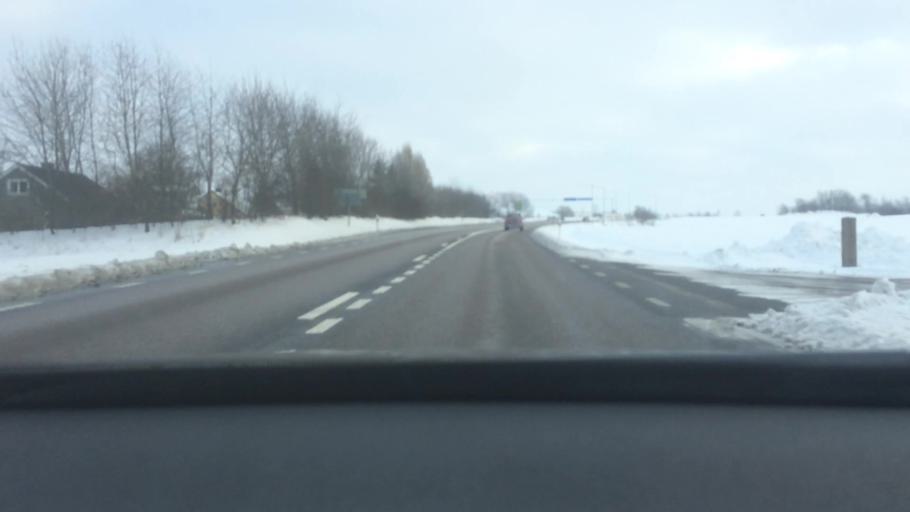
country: SE
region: Vaestra Goetaland
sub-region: Falkopings Kommun
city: Falkoeping
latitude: 58.2282
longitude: 13.5598
